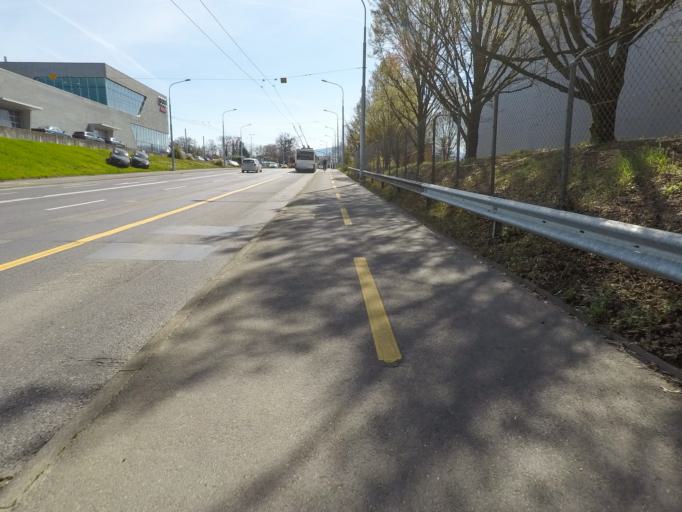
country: CH
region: Geneva
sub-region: Geneva
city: Les Avanchets
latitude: 46.2147
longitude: 6.1015
